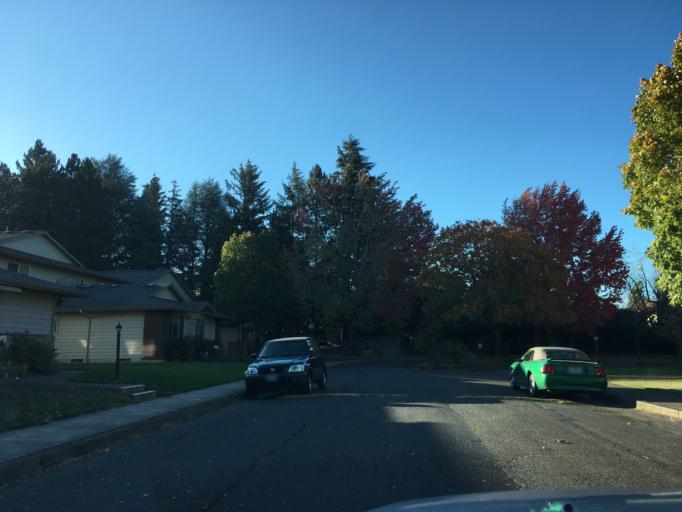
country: US
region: Oregon
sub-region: Multnomah County
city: Wood Village
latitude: 45.5079
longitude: -122.4013
